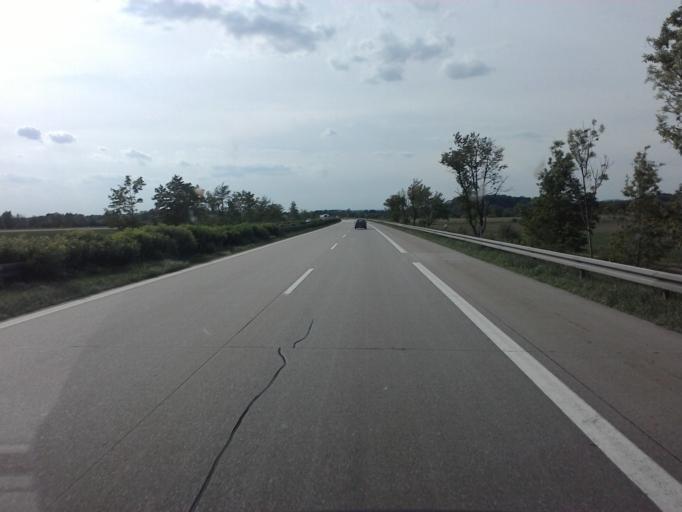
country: DE
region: Bavaria
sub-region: Lower Bavaria
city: Offenberg
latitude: 48.8514
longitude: 12.8801
